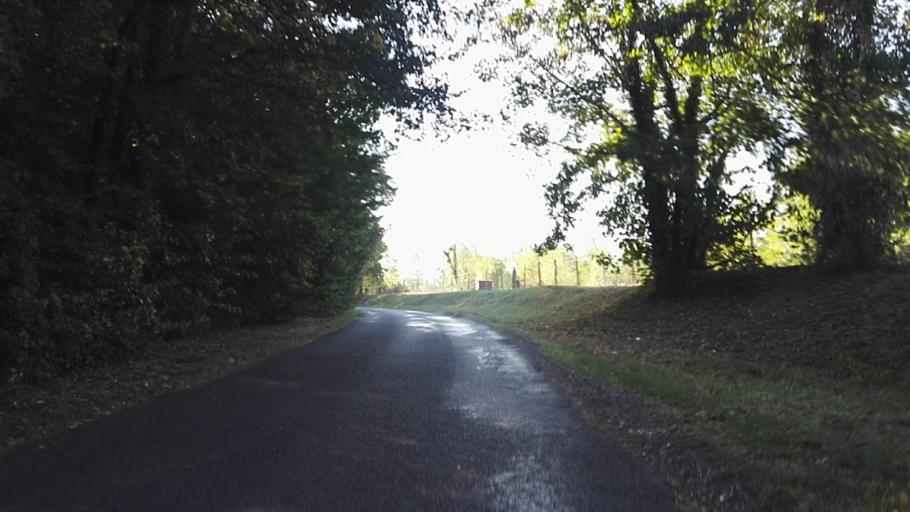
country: FR
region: Haute-Normandie
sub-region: Departement de l'Eure
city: Menilles
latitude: 49.0499
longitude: 1.3360
